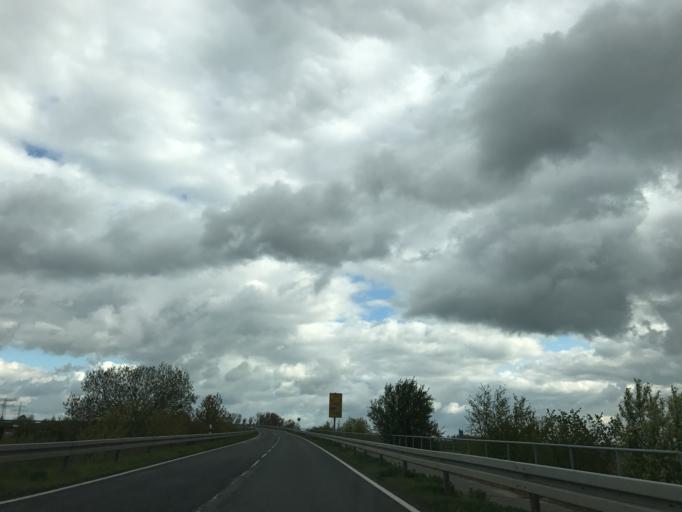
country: DE
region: Brandenburg
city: Wustermark
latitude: 52.5535
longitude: 12.9524
